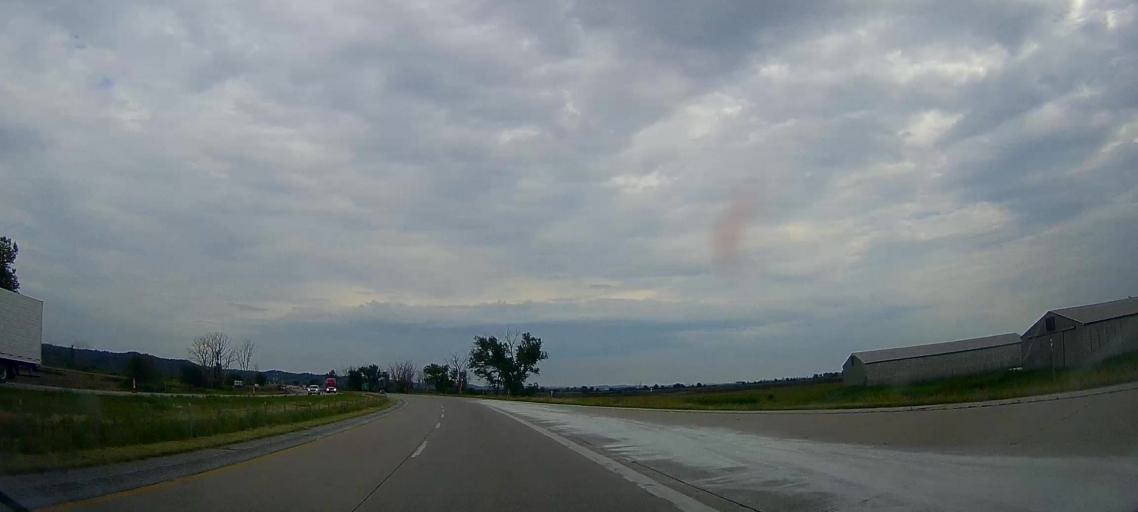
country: US
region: Iowa
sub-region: Harrison County
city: Missouri Valley
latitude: 41.5162
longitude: -95.9163
